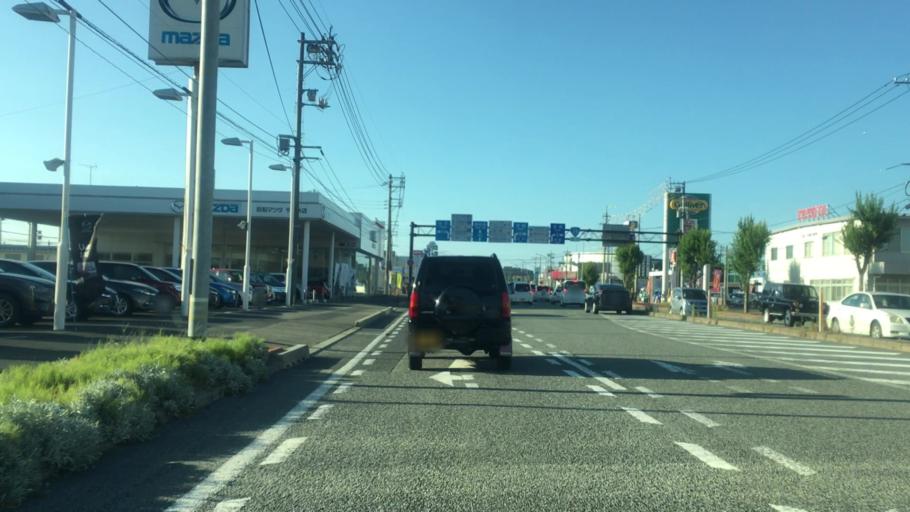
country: JP
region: Tottori
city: Tottori
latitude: 35.5177
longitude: 134.2022
